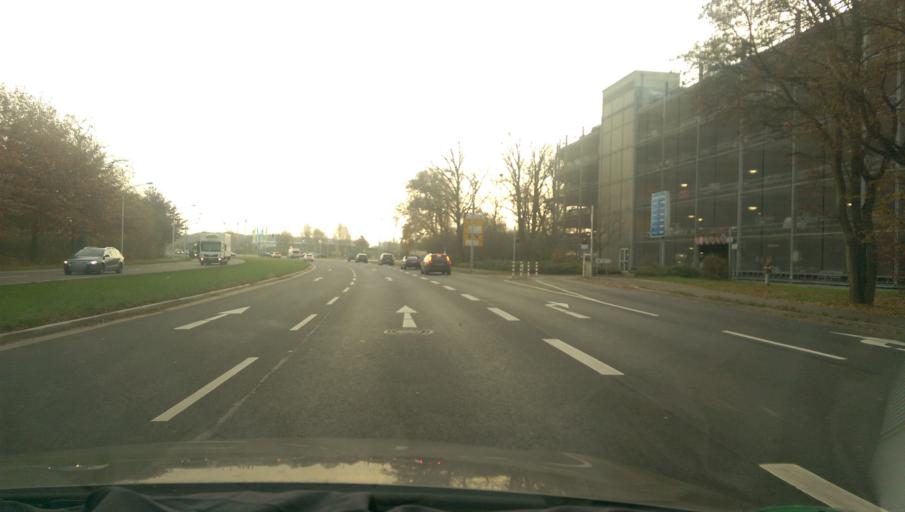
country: DE
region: Lower Saxony
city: Wolfsburg
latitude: 52.4378
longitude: 10.7967
